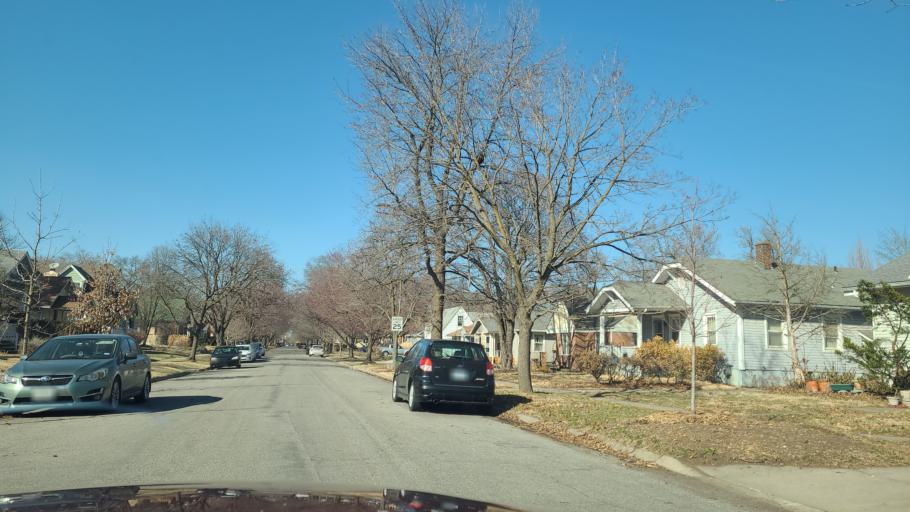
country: US
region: Kansas
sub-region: Douglas County
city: Lawrence
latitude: 38.9466
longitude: -95.2347
